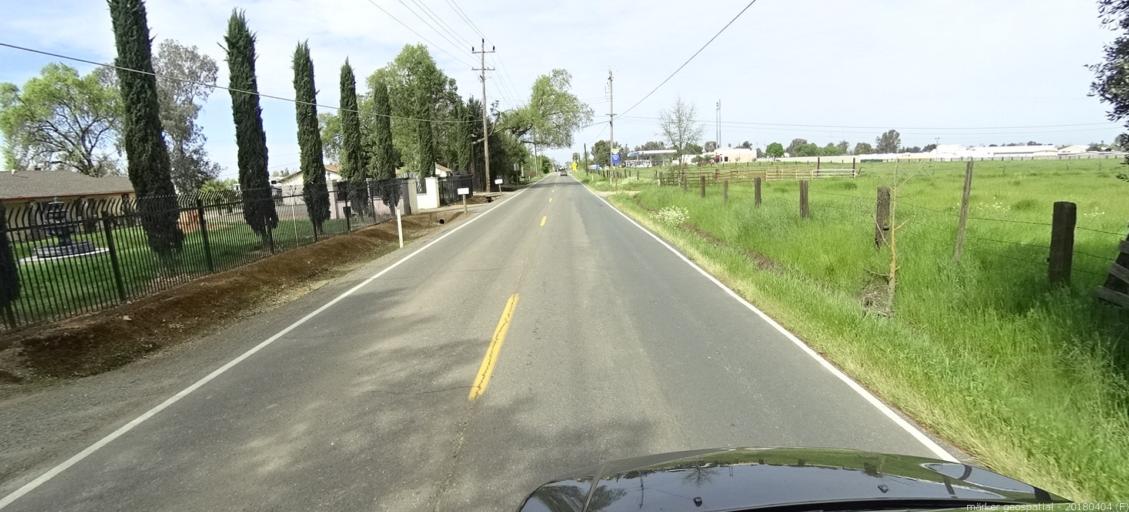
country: US
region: California
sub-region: Sacramento County
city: Galt
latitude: 38.2621
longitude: -121.2940
